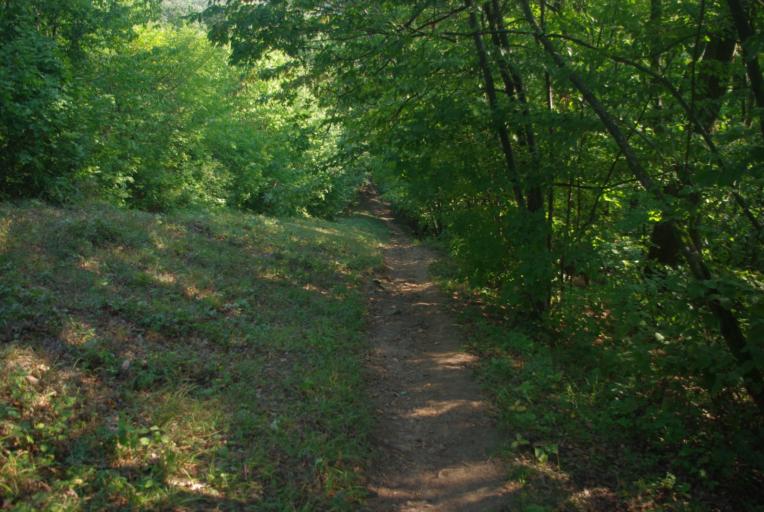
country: HU
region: Budapest
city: Budapest II. keruelet
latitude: 47.5418
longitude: 18.9822
